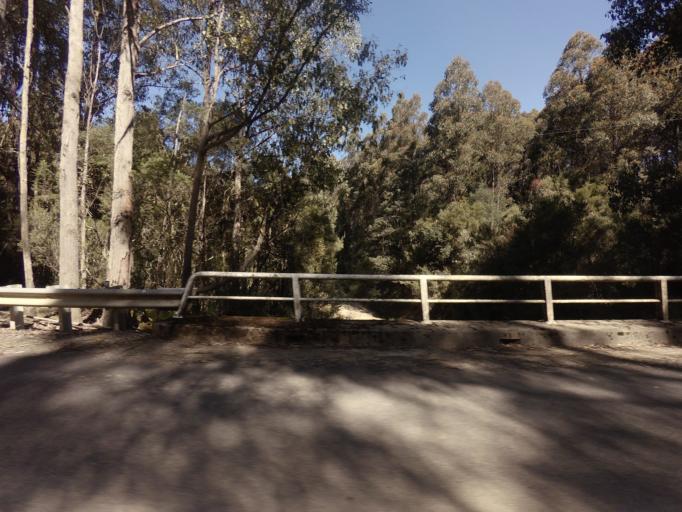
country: AU
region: Tasmania
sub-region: Derwent Valley
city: New Norfolk
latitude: -42.7651
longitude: 146.5949
